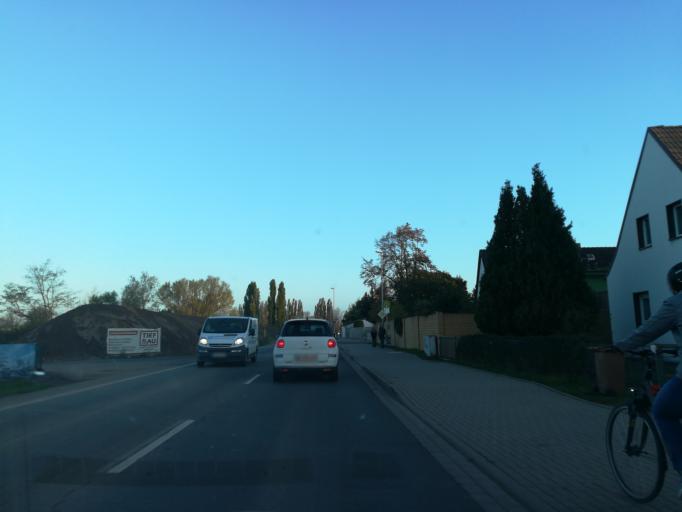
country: DE
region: Saxony-Anhalt
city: Diesdorf
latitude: 52.1349
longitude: 11.5728
